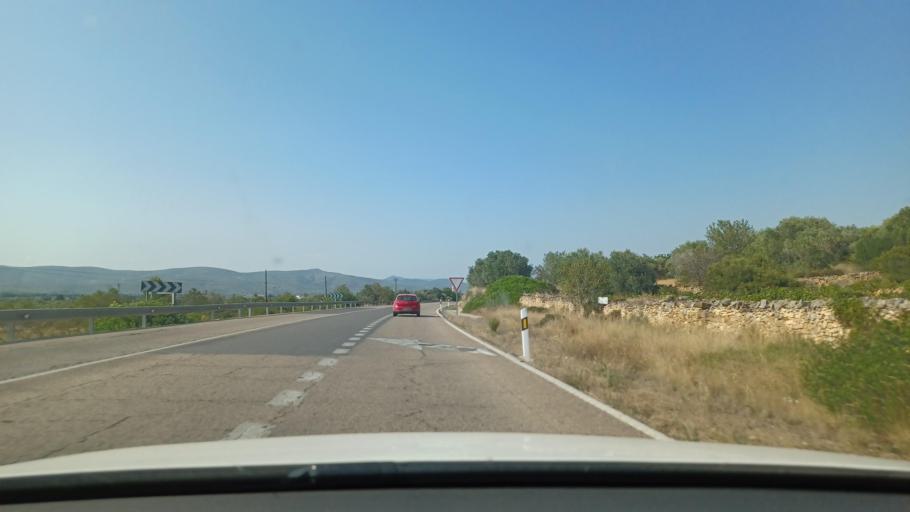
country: ES
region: Valencia
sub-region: Provincia de Castello
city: Alcala de Xivert
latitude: 40.2836
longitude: 0.2247
